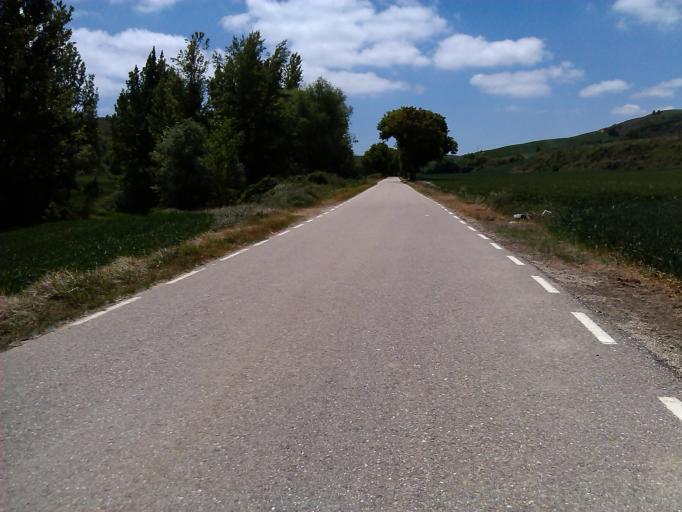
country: ES
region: Castille and Leon
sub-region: Provincia de Burgos
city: Alcocero de Mola
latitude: 42.4436
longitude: -3.3504
